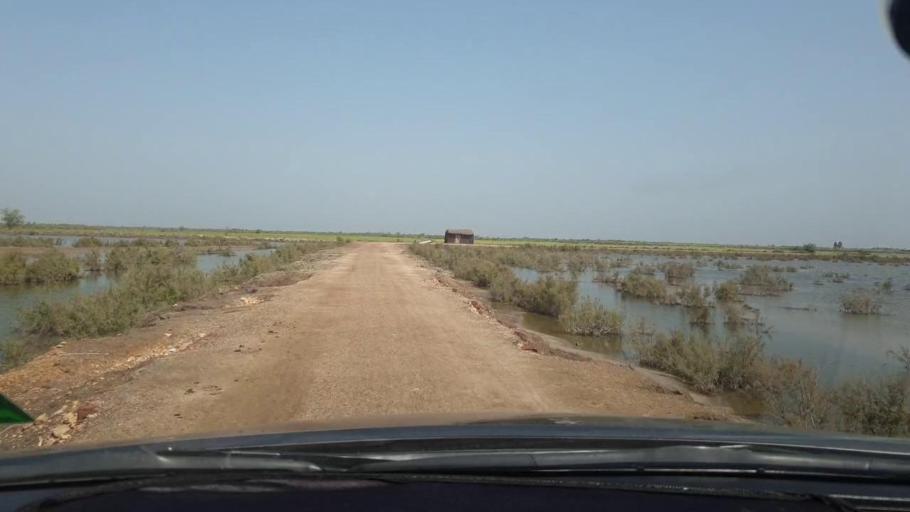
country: PK
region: Sindh
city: Tando Bago
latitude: 24.7924
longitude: 69.0817
